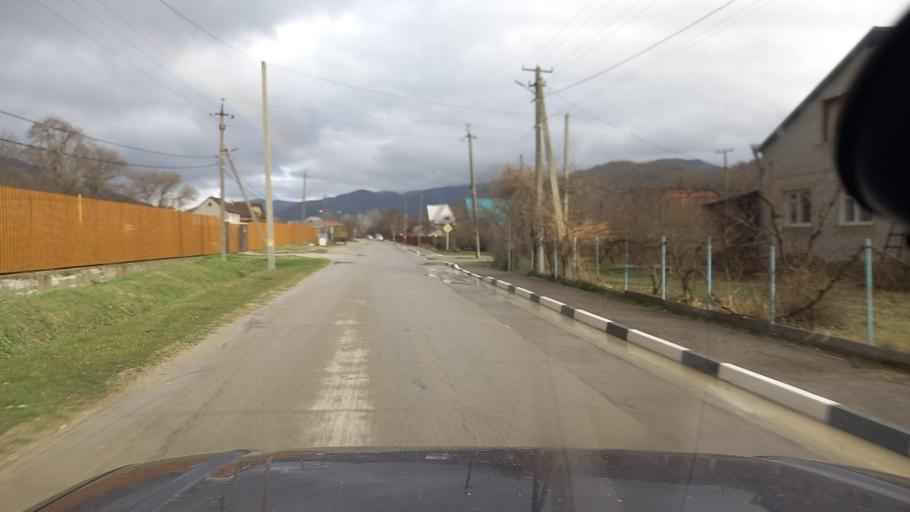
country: RU
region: Krasnodarskiy
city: Pshada
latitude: 44.4783
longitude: 38.4007
